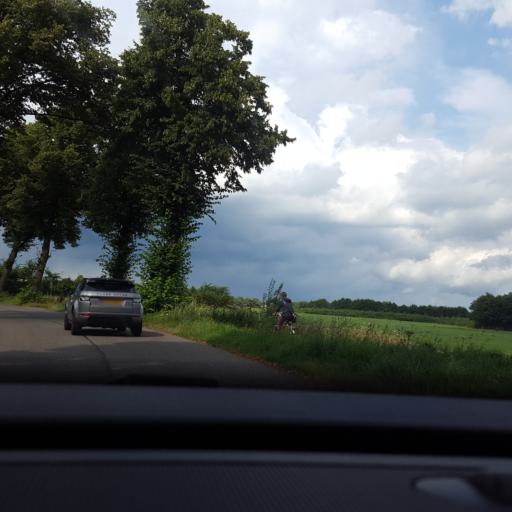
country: NL
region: Gelderland
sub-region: Gemeente Bronckhorst
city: Baak
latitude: 52.0668
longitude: 6.1925
